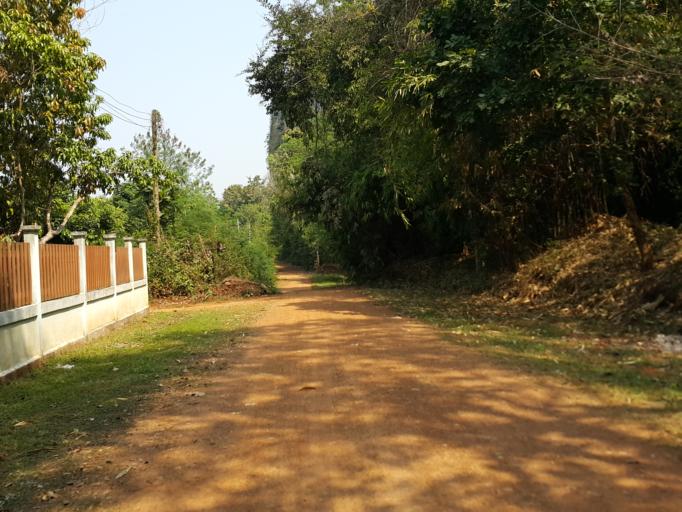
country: TH
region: Sukhothai
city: Thung Saliam
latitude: 17.3062
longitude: 99.5054
